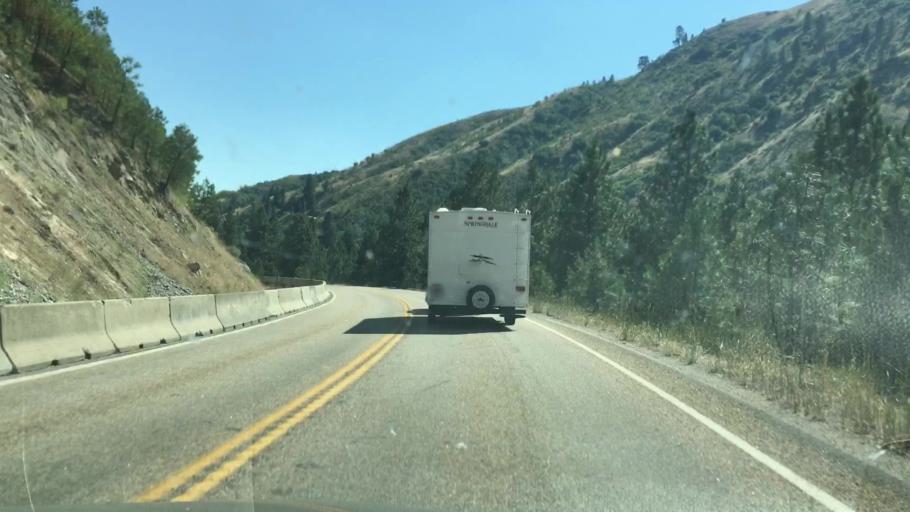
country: US
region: Idaho
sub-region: Boise County
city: Idaho City
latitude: 44.0815
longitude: -116.1209
